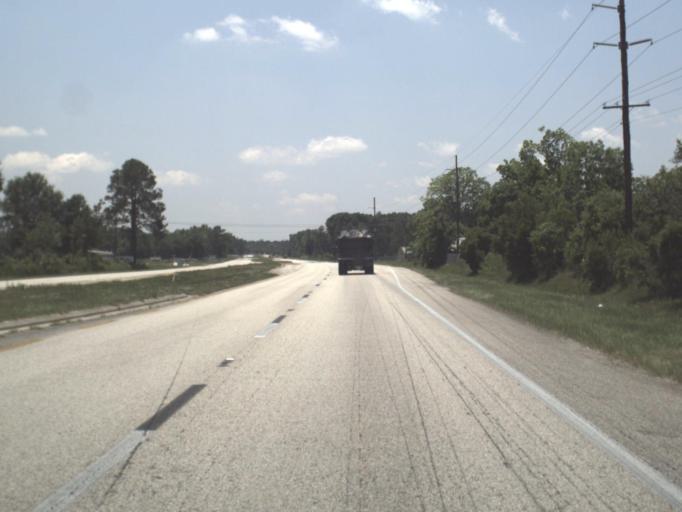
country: US
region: Florida
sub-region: Bradford County
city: Starke
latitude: 29.9990
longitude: -82.0930
